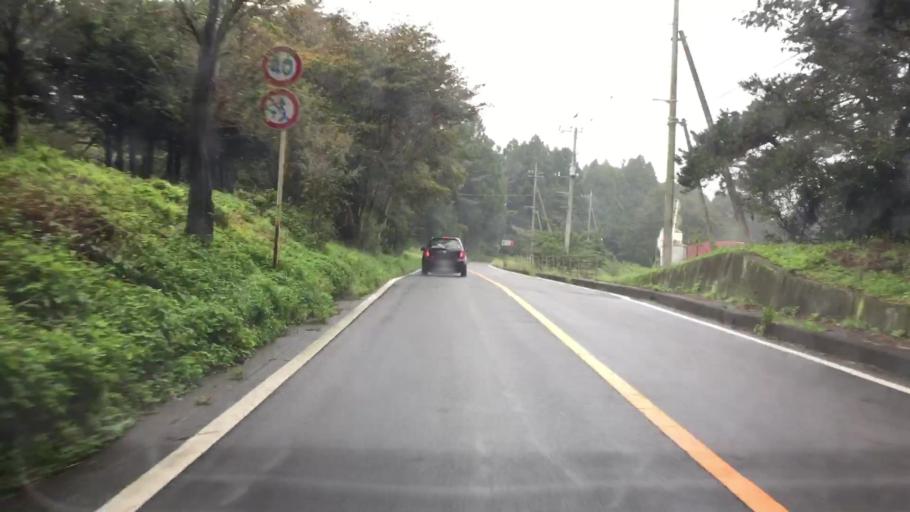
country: JP
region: Yamanashi
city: Fujikawaguchiko
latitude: 35.4003
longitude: 138.6119
